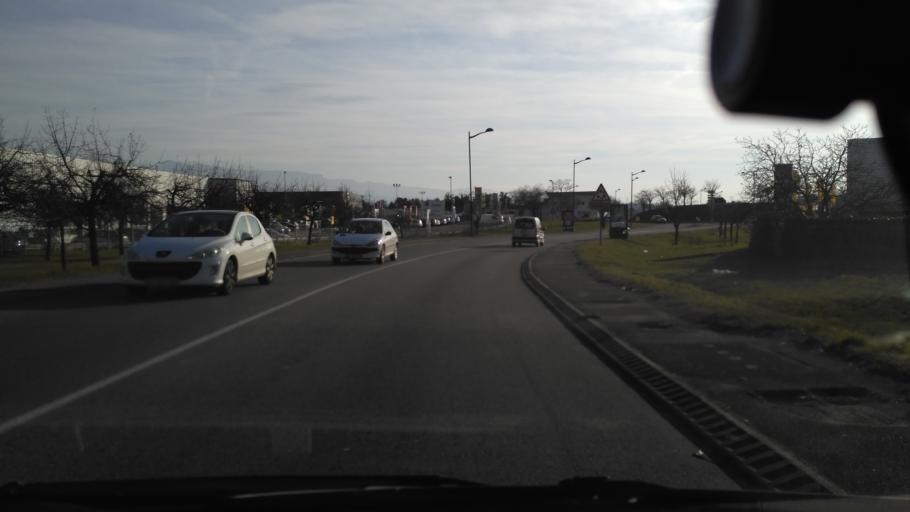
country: FR
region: Rhone-Alpes
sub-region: Departement de la Drome
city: Bourg-de-Peage
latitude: 45.0452
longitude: 5.0845
